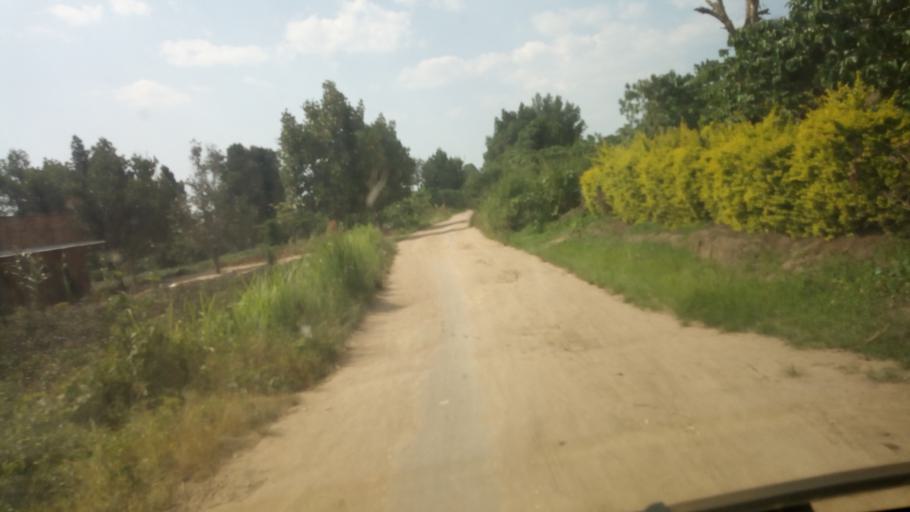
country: UG
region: Western Region
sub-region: Kanungu District
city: Ntungamo
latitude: -0.7840
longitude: 29.6903
